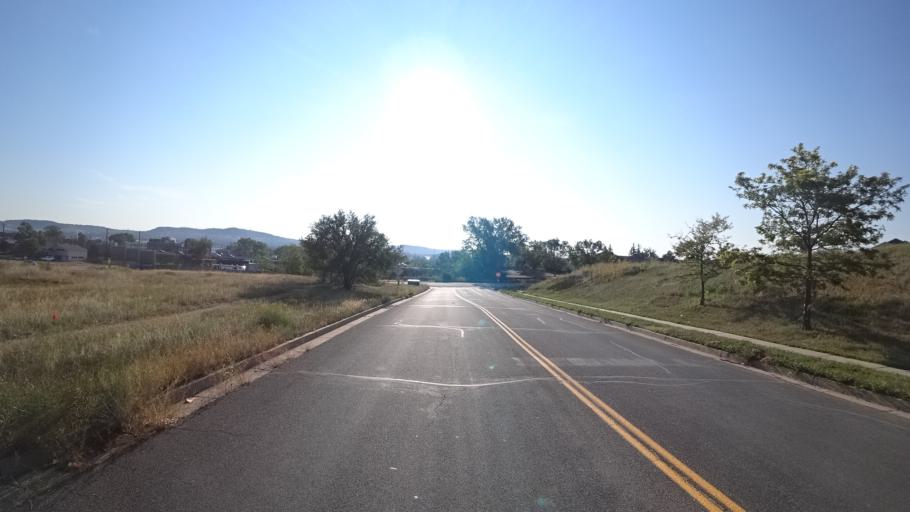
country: US
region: Colorado
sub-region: El Paso County
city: Colorado Springs
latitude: 38.8835
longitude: -104.8381
